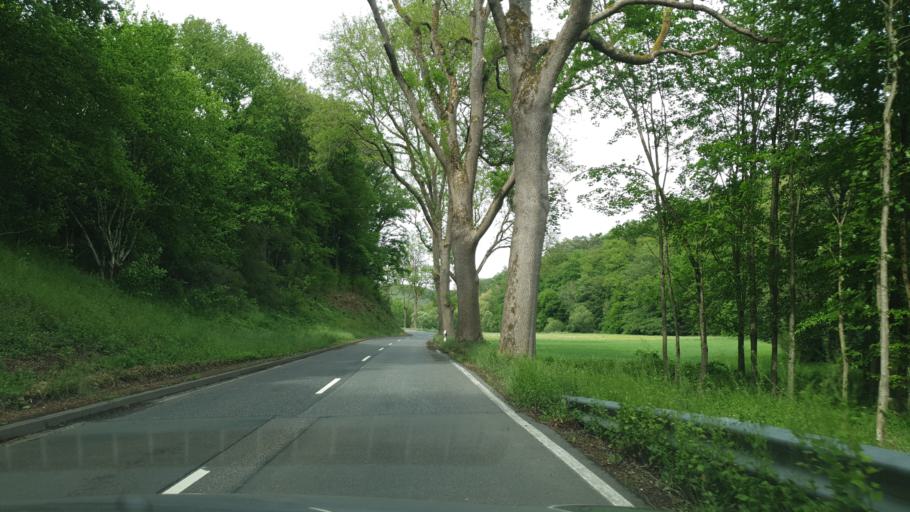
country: DE
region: Rheinland-Pfalz
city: Heilberscheid
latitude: 50.4154
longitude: 7.8706
